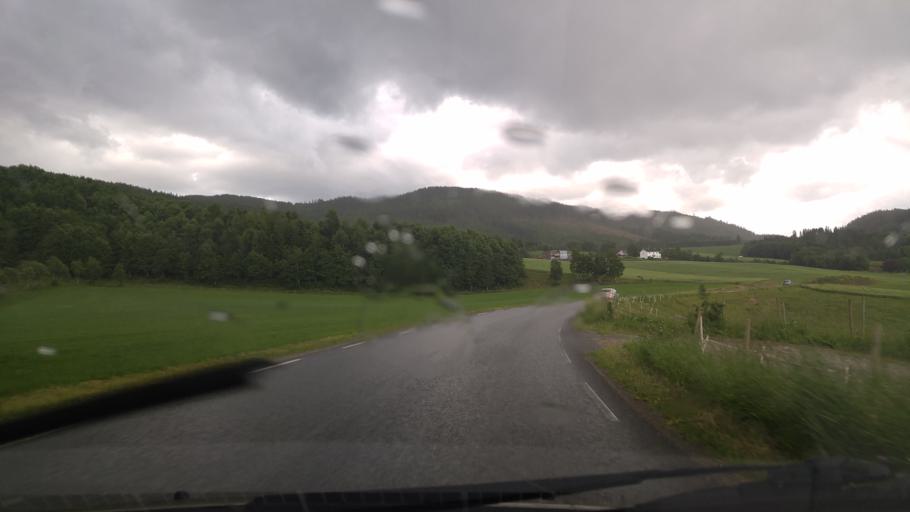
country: NO
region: Nord-Trondelag
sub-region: Levanger
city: Skogn
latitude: 63.6823
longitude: 11.2424
